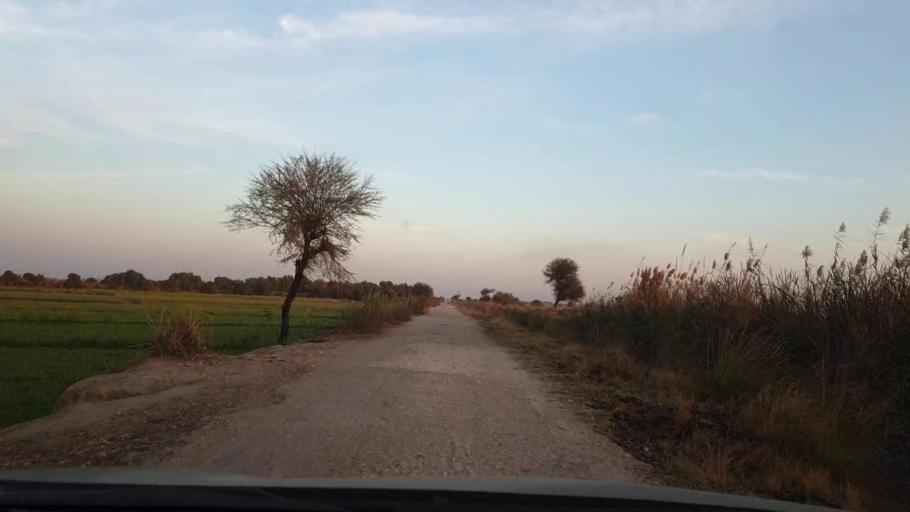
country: PK
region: Sindh
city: Tando Allahyar
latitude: 25.5860
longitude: 68.7191
